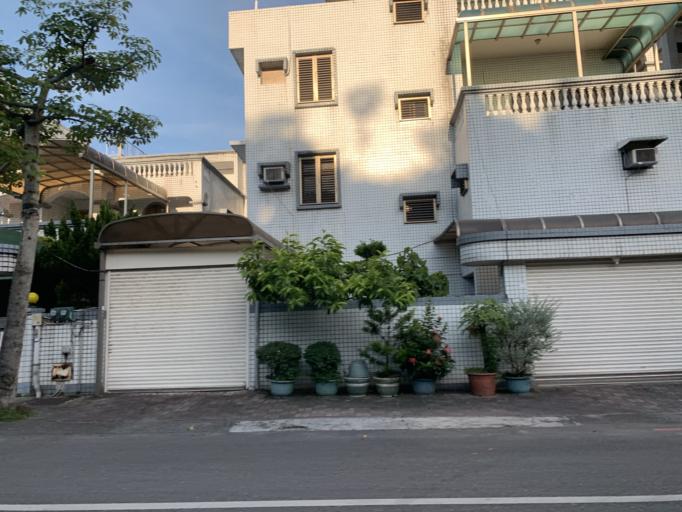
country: TW
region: Taiwan
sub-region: Hualien
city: Hualian
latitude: 24.0050
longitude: 121.6297
